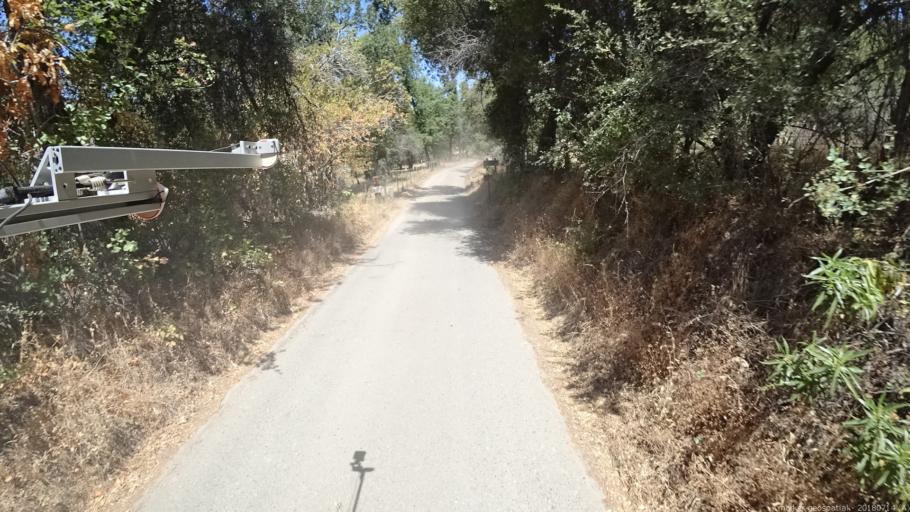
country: US
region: California
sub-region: Madera County
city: Ahwahnee
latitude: 37.3990
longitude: -119.7109
